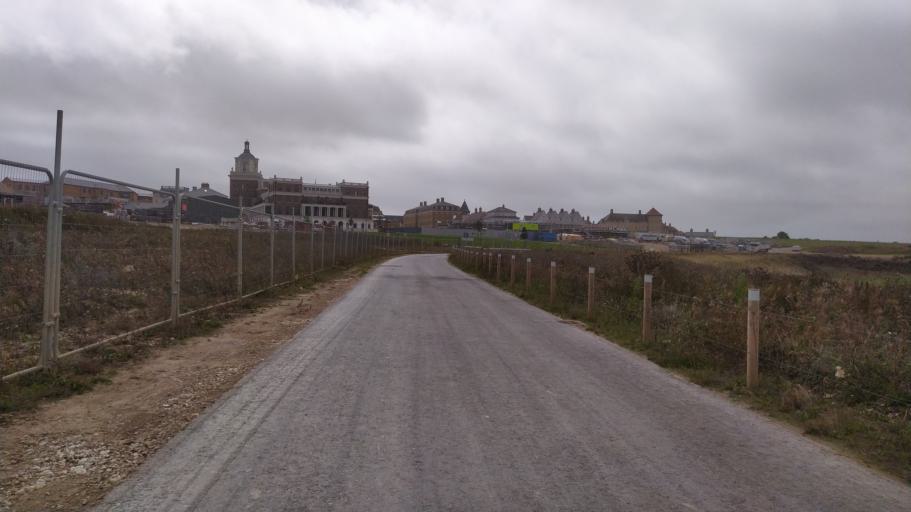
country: GB
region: England
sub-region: Dorset
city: Dorchester
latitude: 50.7184
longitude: -2.4661
